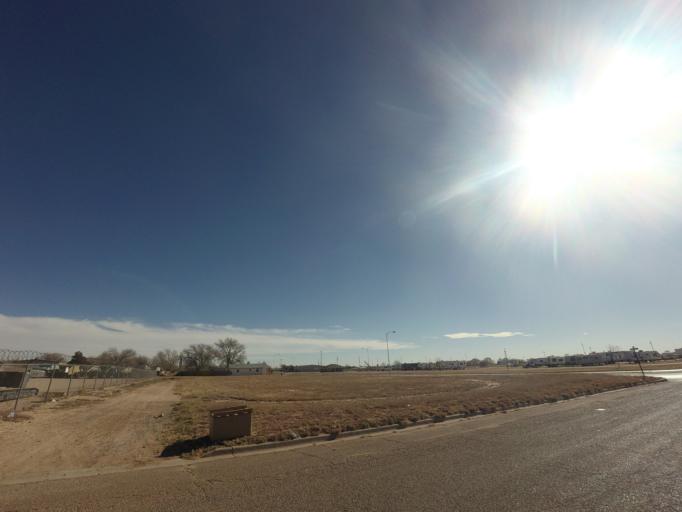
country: US
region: New Mexico
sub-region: Curry County
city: Clovis
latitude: 34.4012
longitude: -103.2366
